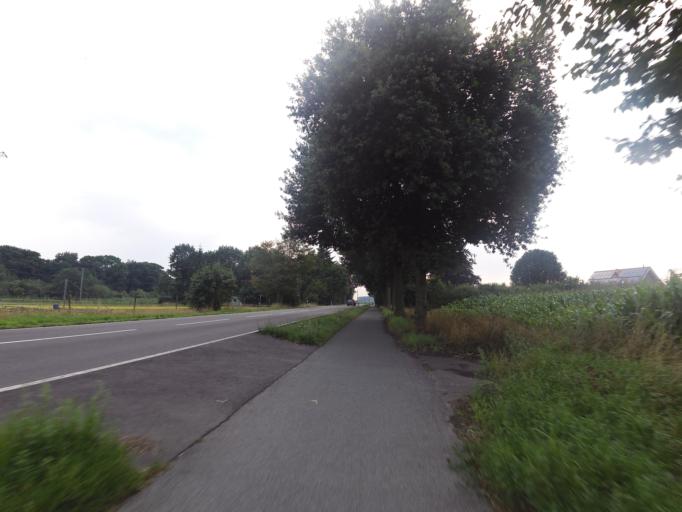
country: NL
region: Gelderland
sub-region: Oude IJsselstreek
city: Gendringen
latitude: 51.8549
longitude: 6.4102
